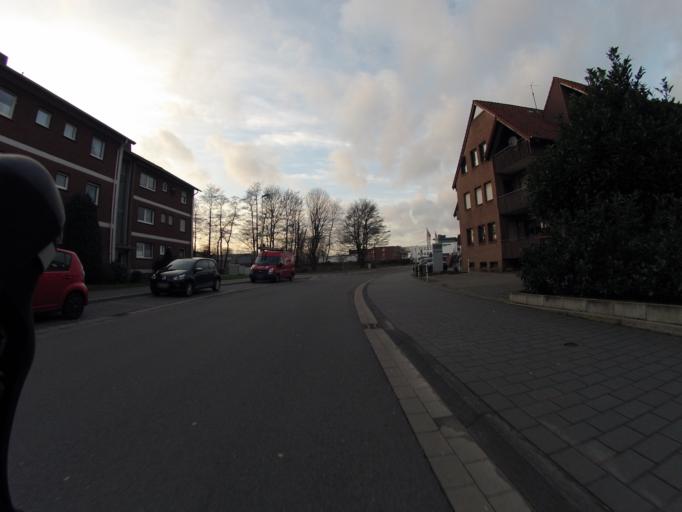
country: DE
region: North Rhine-Westphalia
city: Ibbenburen
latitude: 52.2706
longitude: 7.7307
